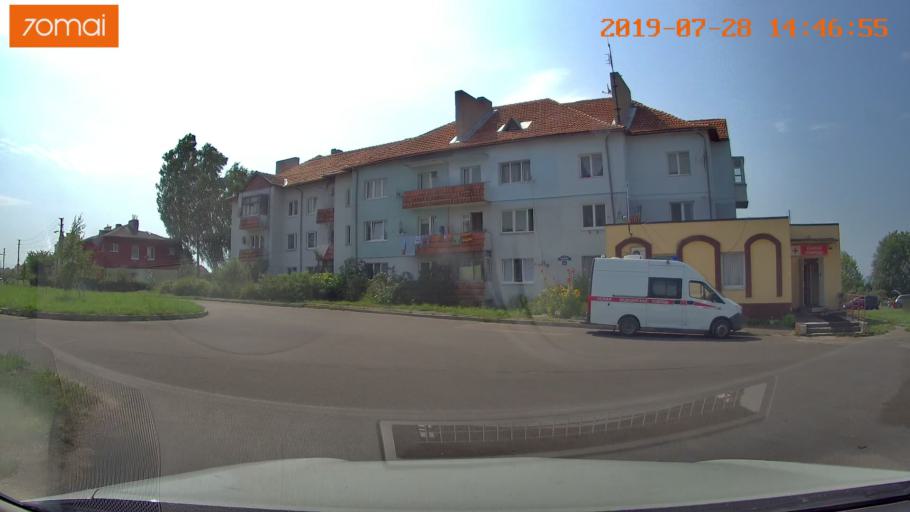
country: RU
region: Kaliningrad
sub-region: Gorod Kaliningrad
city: Yantarnyy
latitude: 54.8756
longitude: 19.9395
